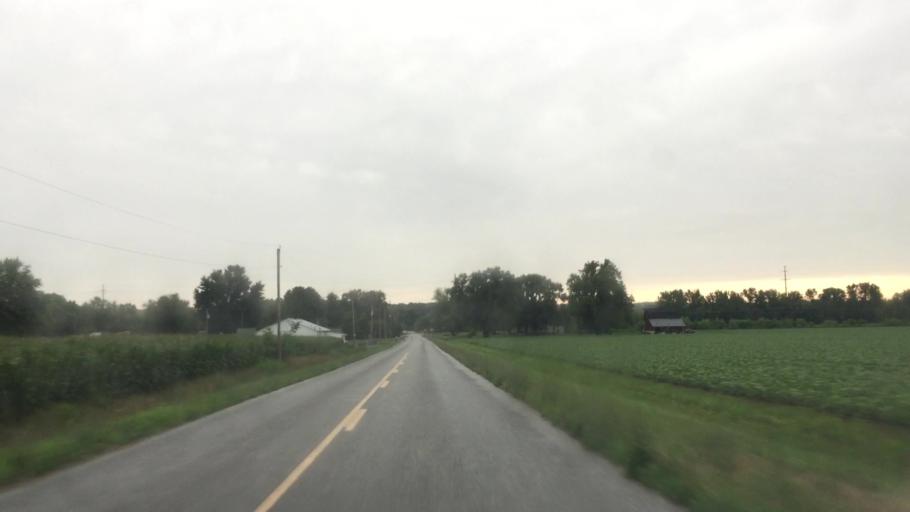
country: US
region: Iowa
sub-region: Lee County
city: Fort Madison
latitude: 40.6142
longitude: -91.2819
